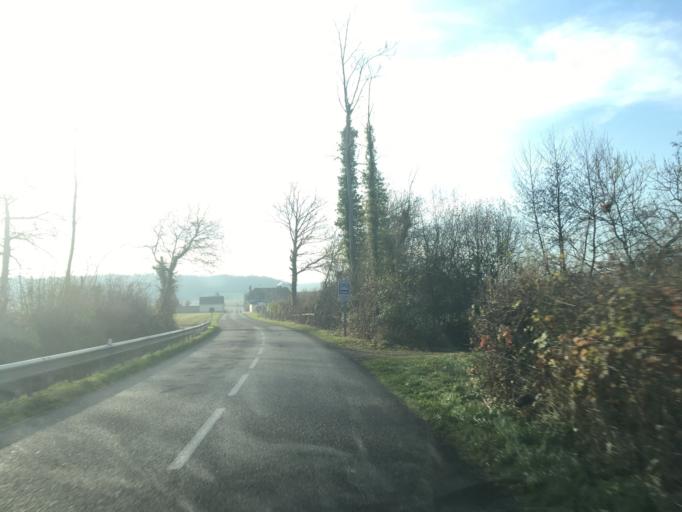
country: FR
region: Haute-Normandie
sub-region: Departement de l'Eure
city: Menilles
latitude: 49.0475
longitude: 1.3119
